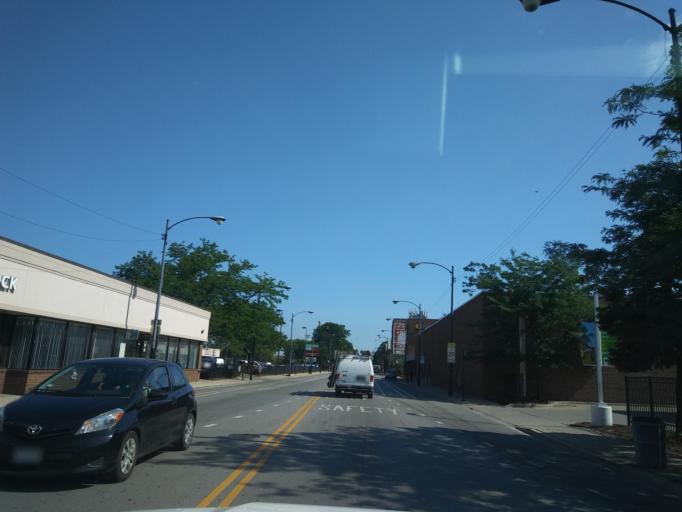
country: US
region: Illinois
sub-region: Cook County
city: Chicago
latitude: 41.8383
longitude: -87.6463
